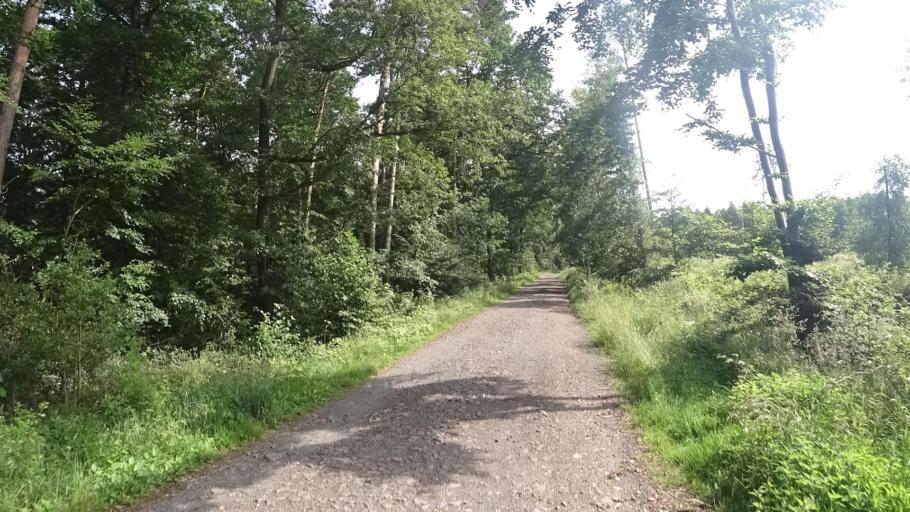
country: DE
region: Rheinland-Pfalz
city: Dernau
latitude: 50.5486
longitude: 7.0490
